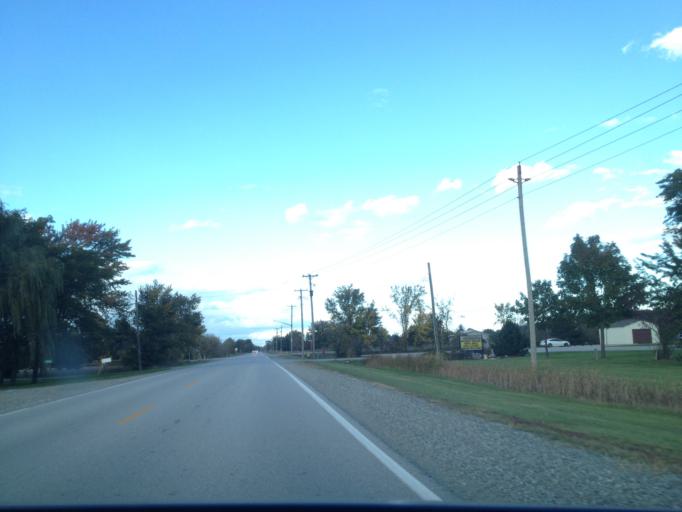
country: US
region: Michigan
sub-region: Wayne County
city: Grosse Pointe
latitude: 42.1504
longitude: -82.7326
